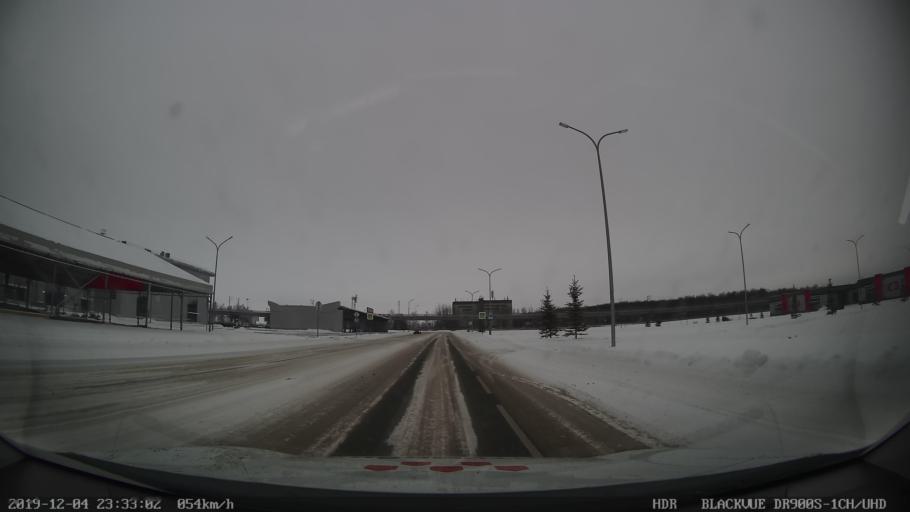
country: RU
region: Tatarstan
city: Stolbishchi
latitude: 55.6134
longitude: 49.2960
